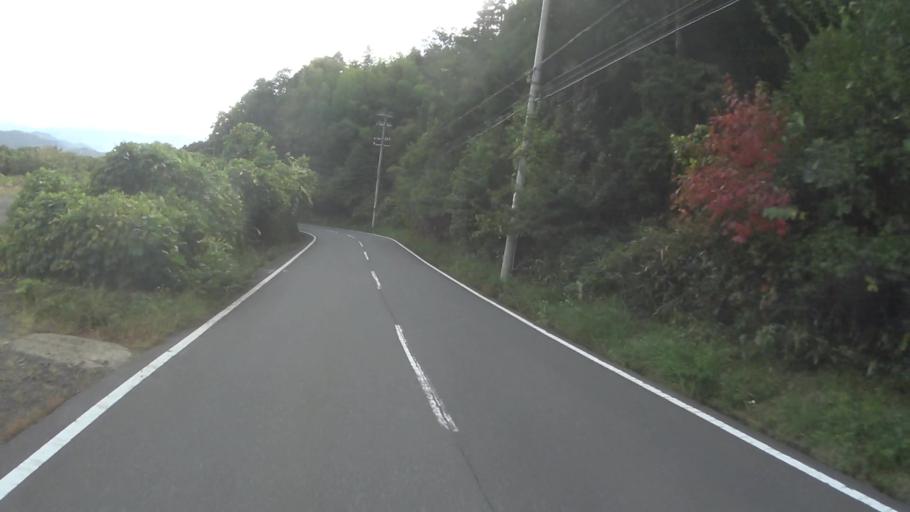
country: JP
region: Kyoto
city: Maizuru
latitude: 35.5285
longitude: 135.3919
